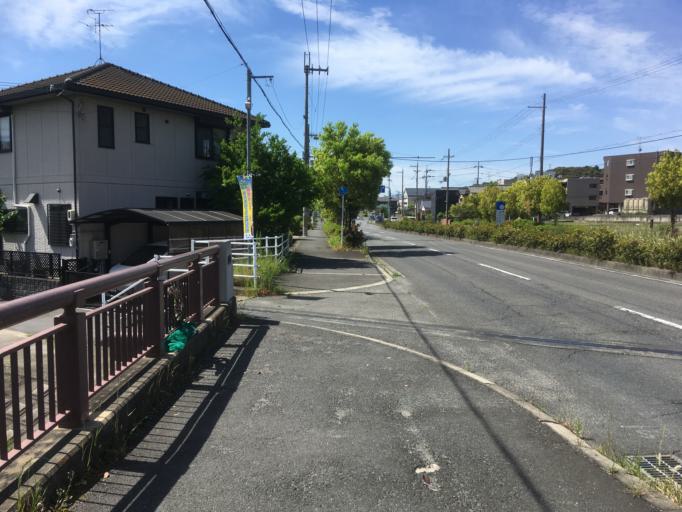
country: JP
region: Nara
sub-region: Ikoma-shi
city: Ikoma
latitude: 34.6781
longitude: 135.7063
